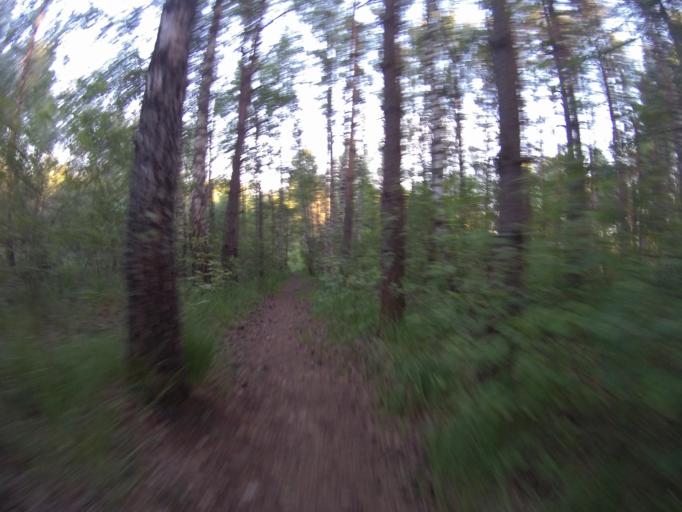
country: RU
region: Vladimir
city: Kommunar
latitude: 56.1116
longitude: 40.4605
